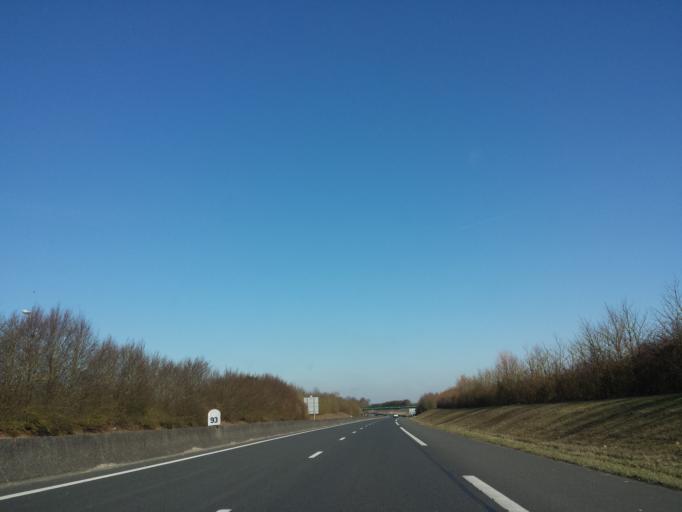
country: FR
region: Picardie
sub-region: Departement de l'Oise
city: Breteuil
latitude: 49.6089
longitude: 2.2062
